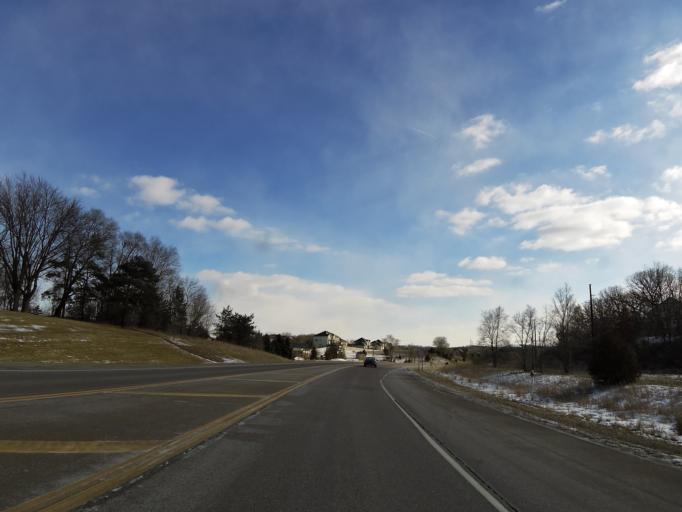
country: US
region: Minnesota
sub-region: Dakota County
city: Eagan
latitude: 44.8158
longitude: -93.1013
